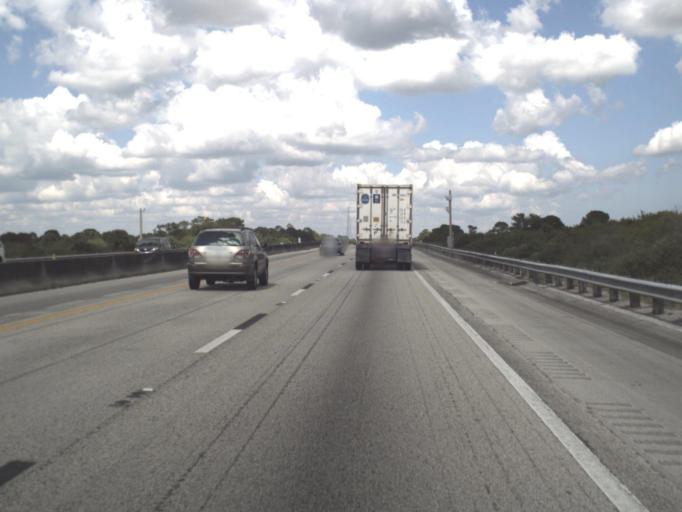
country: US
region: Florida
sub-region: Martin County
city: Port Salerno
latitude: 27.0639
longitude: -80.2431
